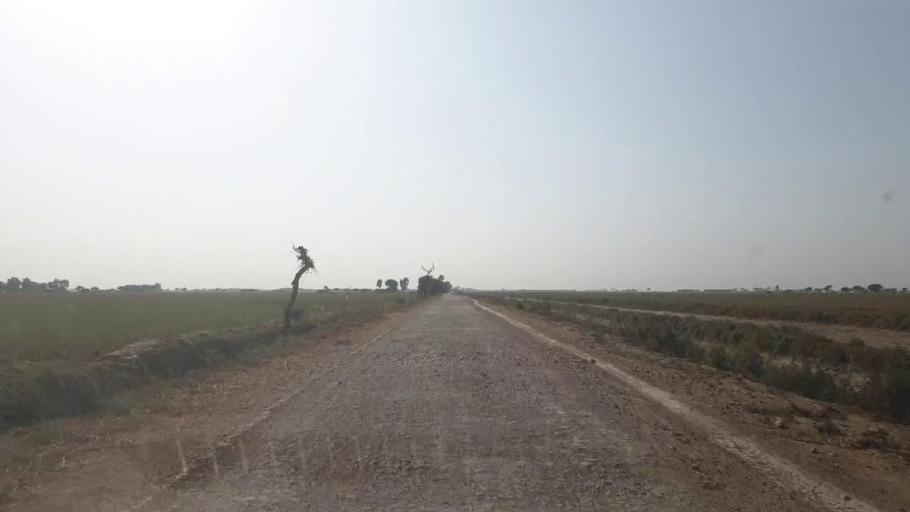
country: PK
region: Sindh
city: Kario
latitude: 24.5765
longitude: 68.5229
